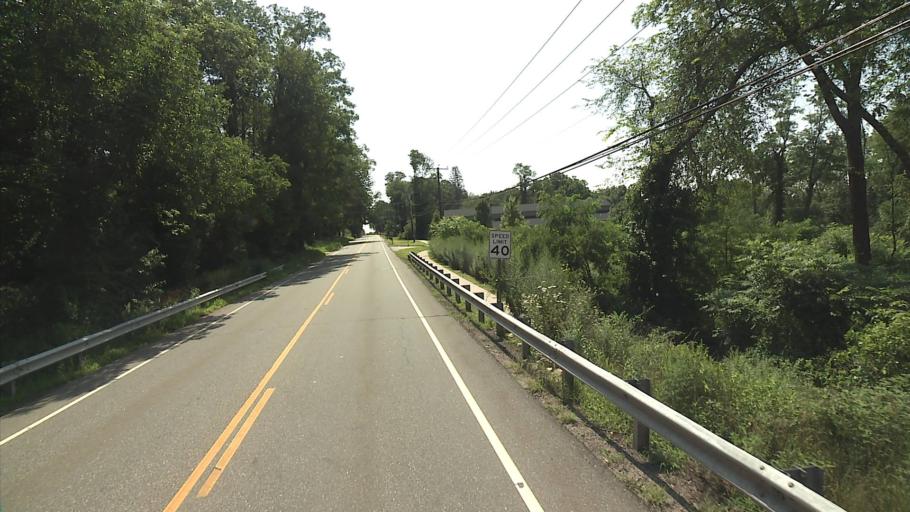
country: US
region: Connecticut
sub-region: New London County
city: Colchester
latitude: 41.5654
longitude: -72.3218
